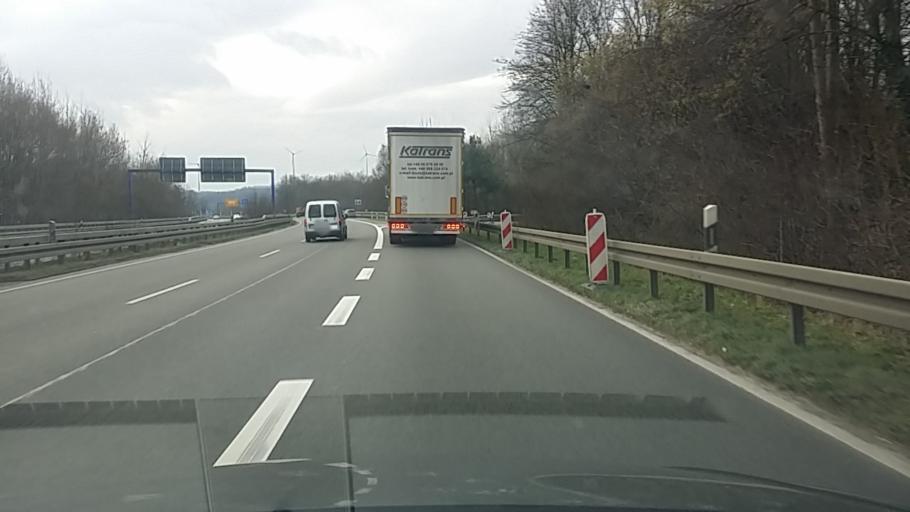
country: DE
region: Lower Saxony
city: Wallenhorst
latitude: 52.3435
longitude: 8.0196
